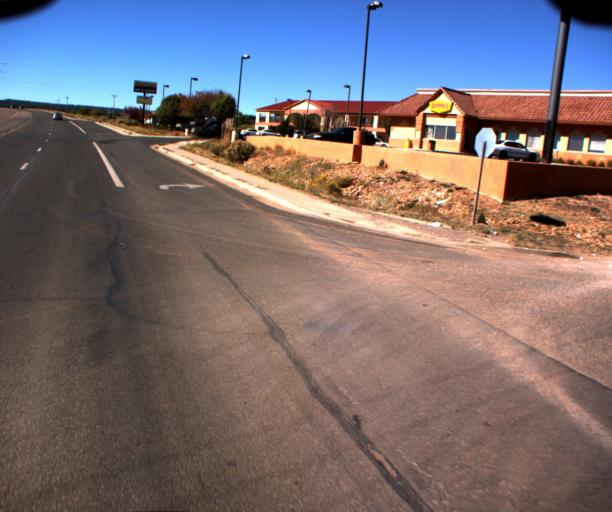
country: US
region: Arizona
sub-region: Apache County
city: Saint Michaels
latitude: 35.6582
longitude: -109.1129
